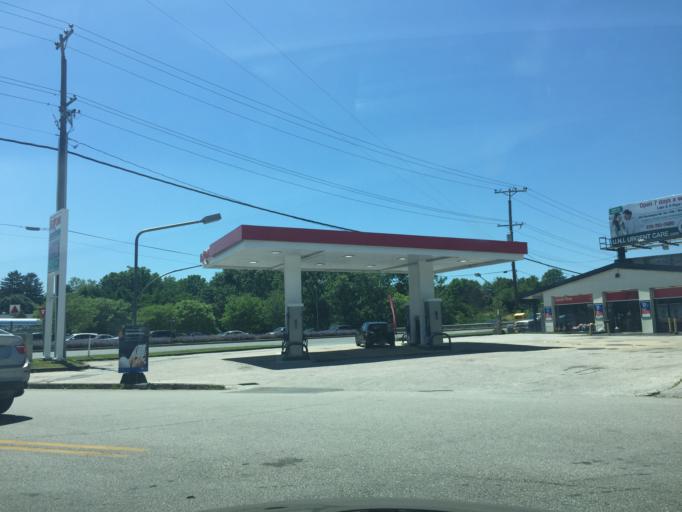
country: US
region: Maryland
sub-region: Carroll County
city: Westminster
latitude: 39.5892
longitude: -76.9945
